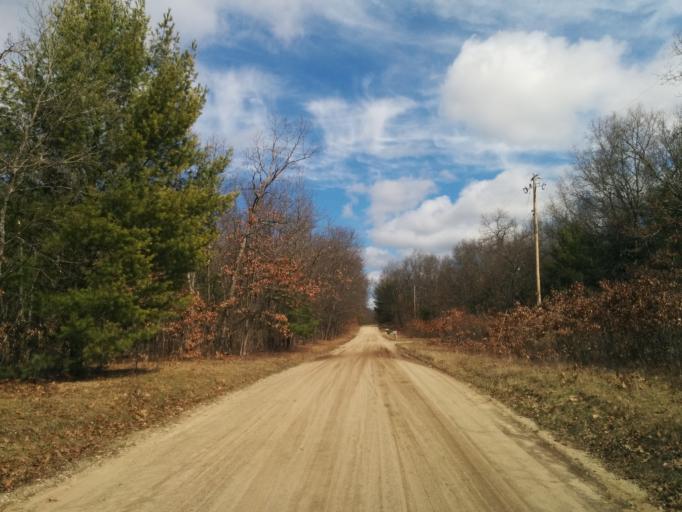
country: US
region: Michigan
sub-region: Newaygo County
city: Newaygo
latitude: 43.4299
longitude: -85.7275
